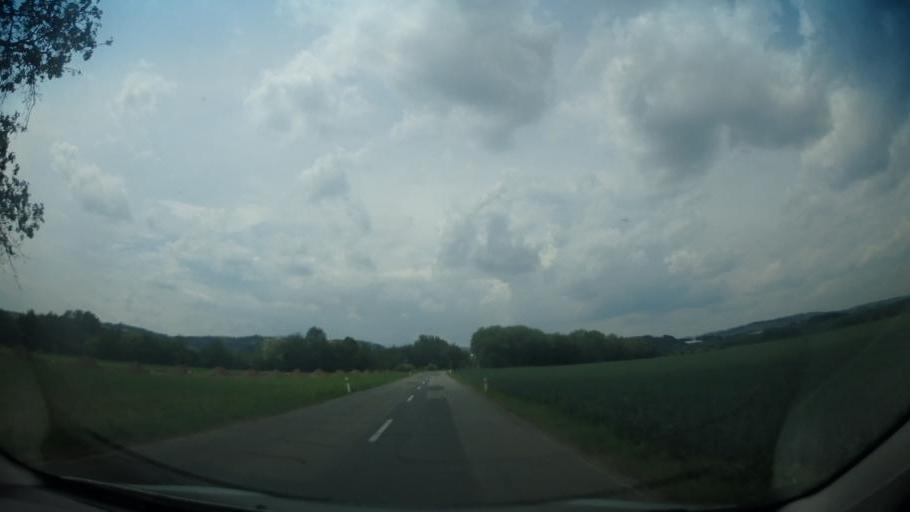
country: CZ
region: South Moravian
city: Lysice
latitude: 49.4396
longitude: 16.5611
